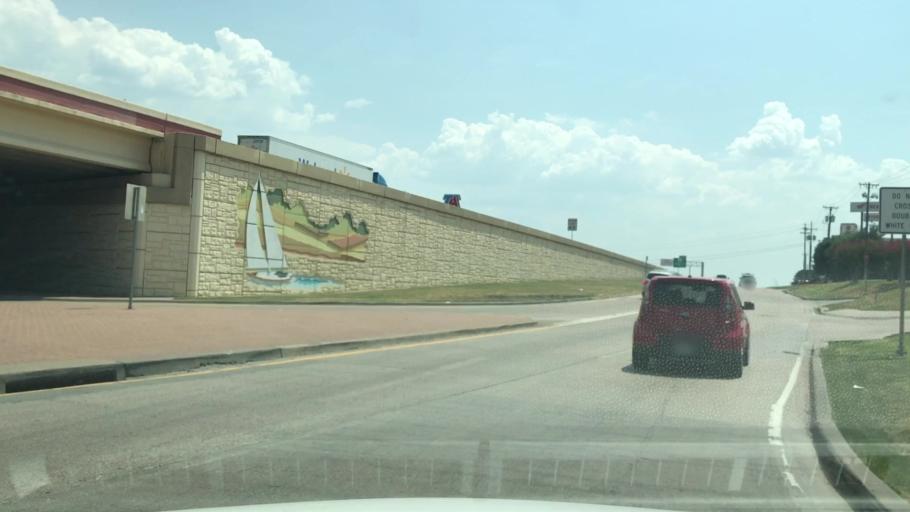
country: US
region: Texas
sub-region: Rockwall County
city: Rockwall
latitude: 32.9094
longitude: -96.4505
